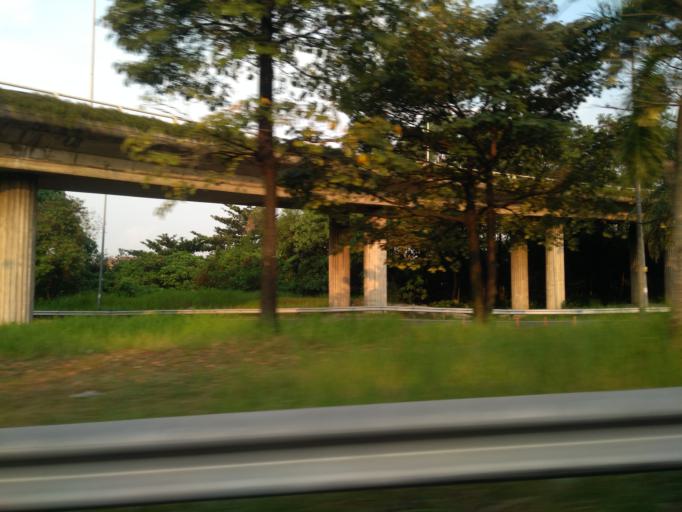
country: MY
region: Kuala Lumpur
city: Kuala Lumpur
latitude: 3.1025
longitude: 101.6982
